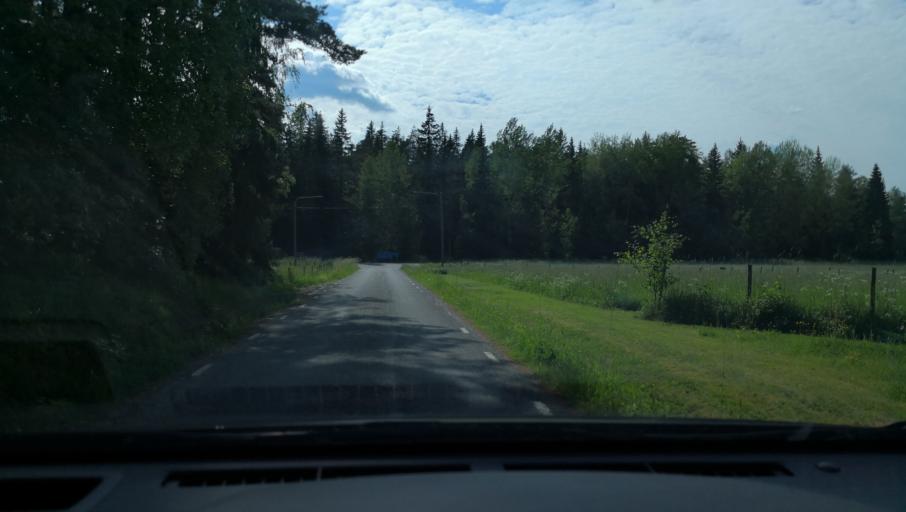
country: SE
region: Uppsala
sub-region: Enkopings Kommun
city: Orsundsbro
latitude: 59.8419
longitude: 17.1881
